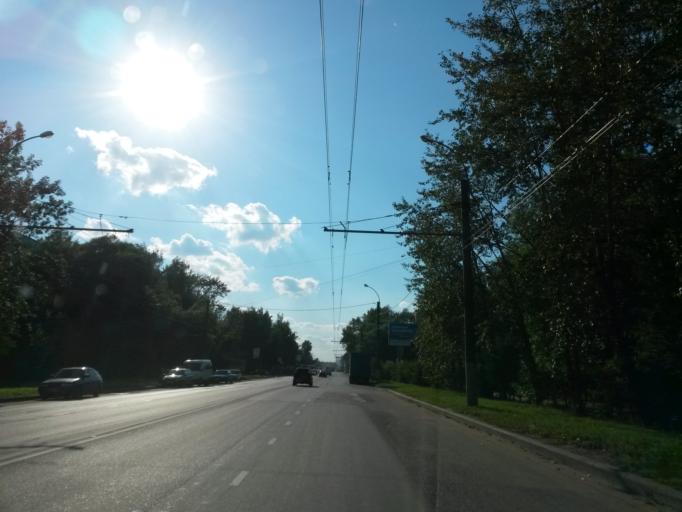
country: RU
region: Ivanovo
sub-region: Gorod Ivanovo
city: Ivanovo
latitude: 56.9575
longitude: 40.9923
